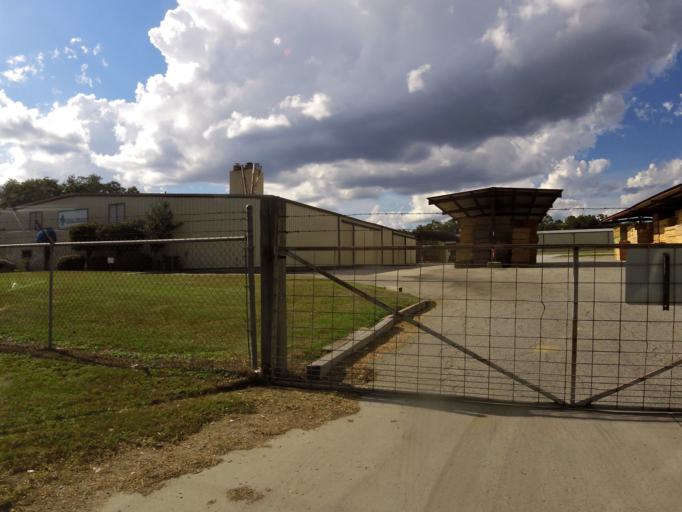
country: US
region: Georgia
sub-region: Lowndes County
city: Valdosta
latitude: 30.8110
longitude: -83.2884
